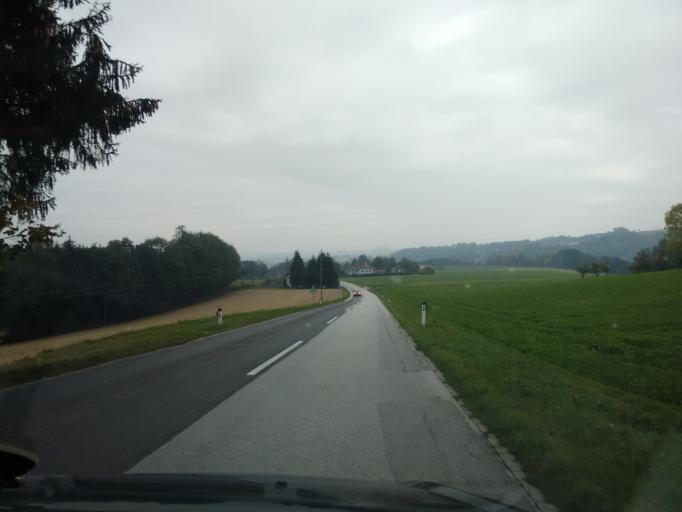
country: AT
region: Upper Austria
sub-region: Politischer Bezirk Kirchdorf an der Krems
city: Kremsmunster
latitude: 48.0472
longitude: 14.1109
